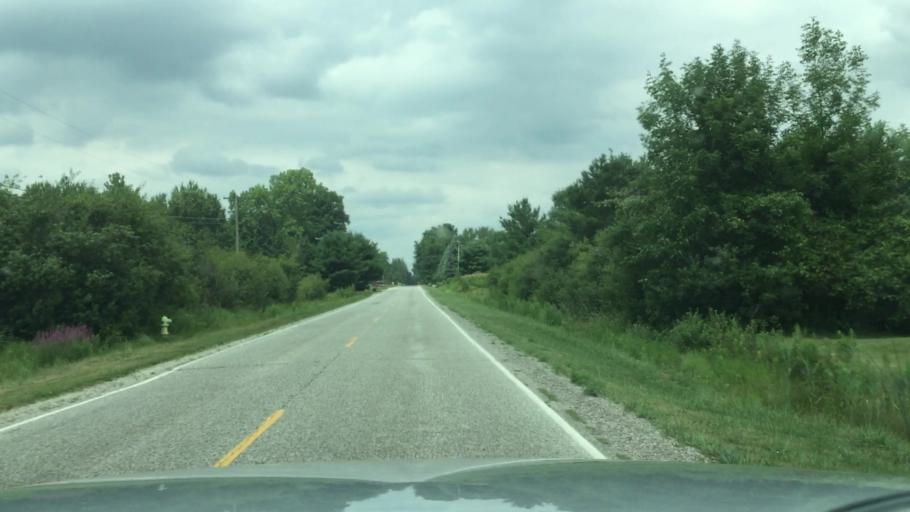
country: US
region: Michigan
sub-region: Saginaw County
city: Bridgeport
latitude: 43.3146
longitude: -83.8946
